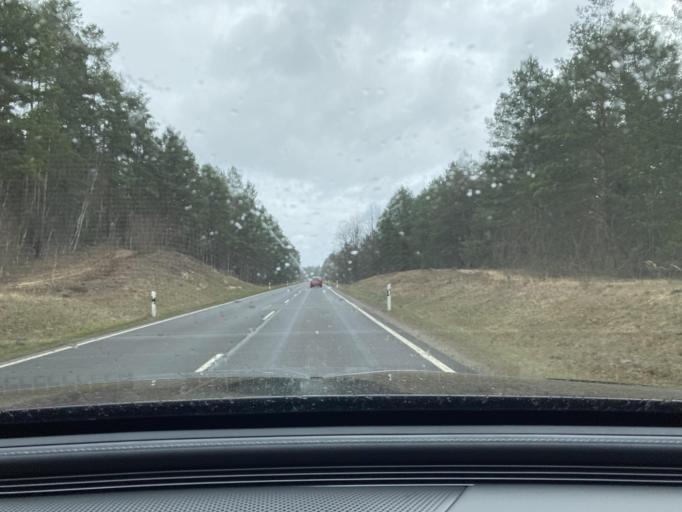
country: DE
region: Saxony
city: Weisskeissel
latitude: 51.4491
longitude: 14.6774
